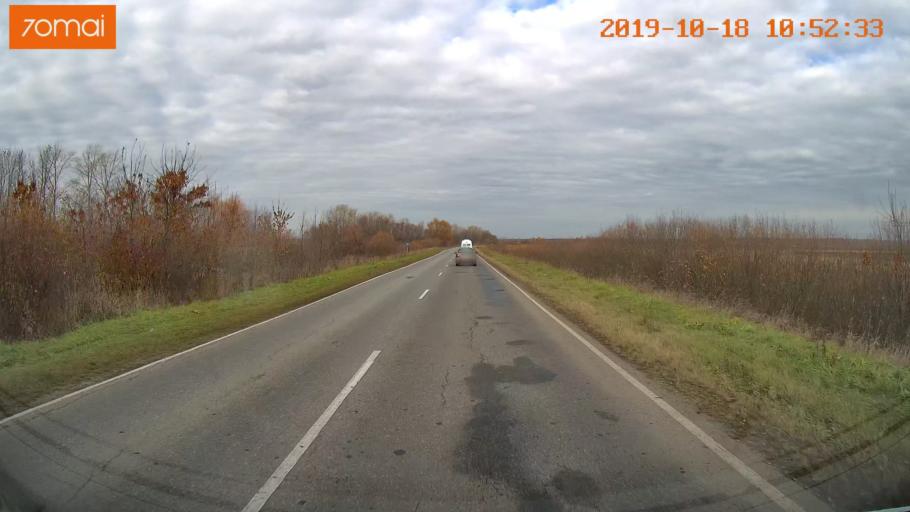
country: RU
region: Tula
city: Yepifan'
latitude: 53.7683
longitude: 38.6502
